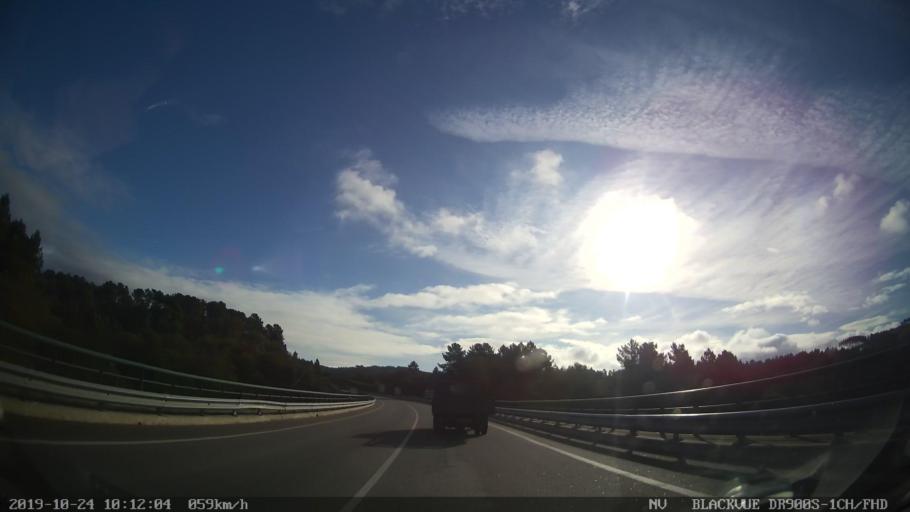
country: PT
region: Vila Real
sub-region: Sabrosa
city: Vilela
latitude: 41.2622
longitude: -7.6576
